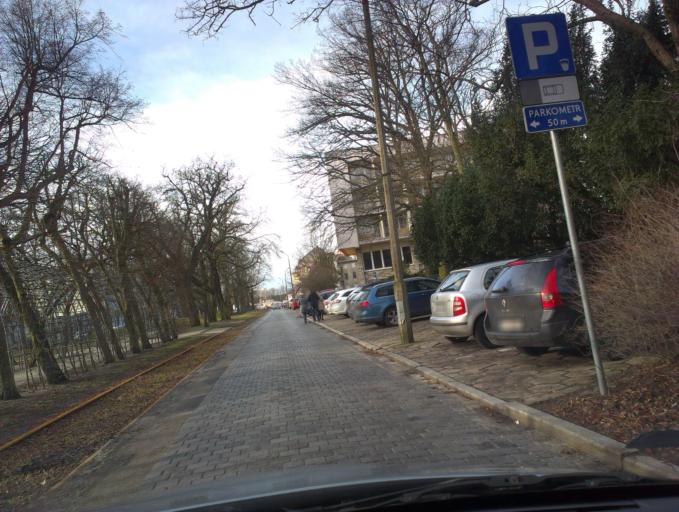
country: PL
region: West Pomeranian Voivodeship
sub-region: Powiat kolobrzeski
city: Kolobrzeg
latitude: 54.1838
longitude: 15.5595
